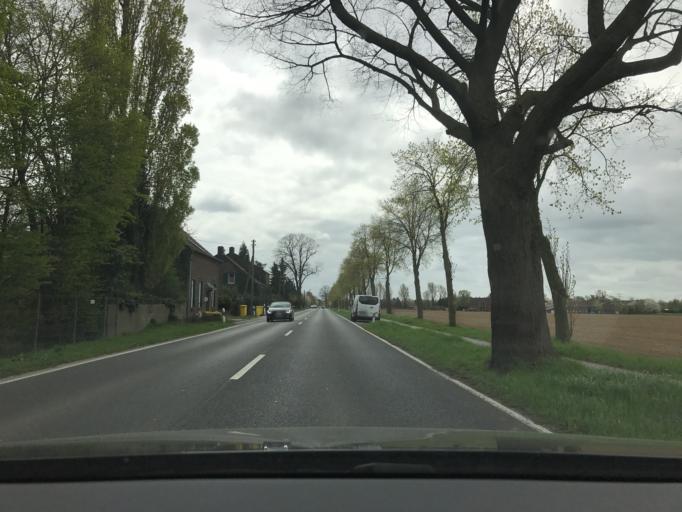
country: DE
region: North Rhine-Westphalia
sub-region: Regierungsbezirk Dusseldorf
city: Kaarst
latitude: 51.2837
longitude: 6.6098
